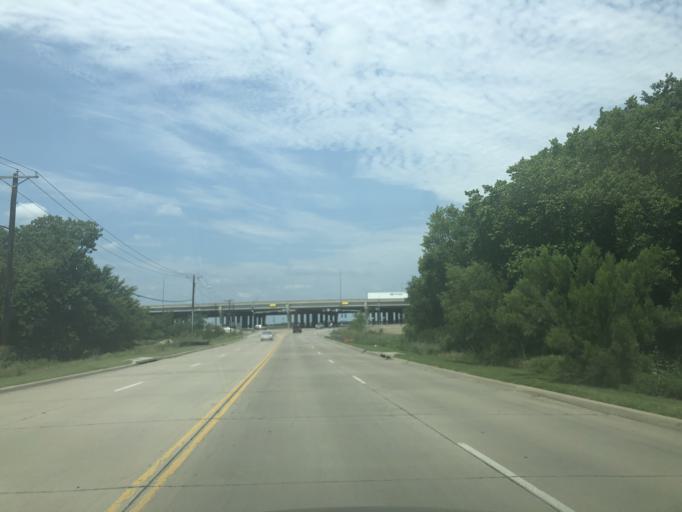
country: US
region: Texas
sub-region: Dallas County
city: Grand Prairie
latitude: 32.7287
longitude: -97.0171
